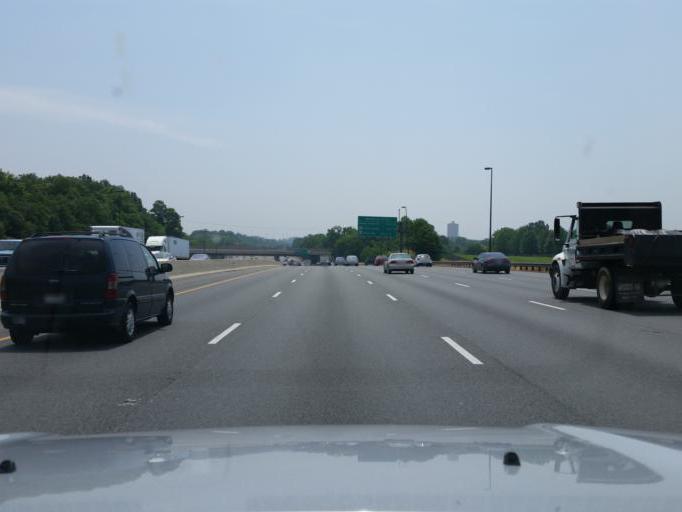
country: US
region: Maryland
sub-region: Montgomery County
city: Gaithersburg
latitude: 39.1345
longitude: -77.2093
